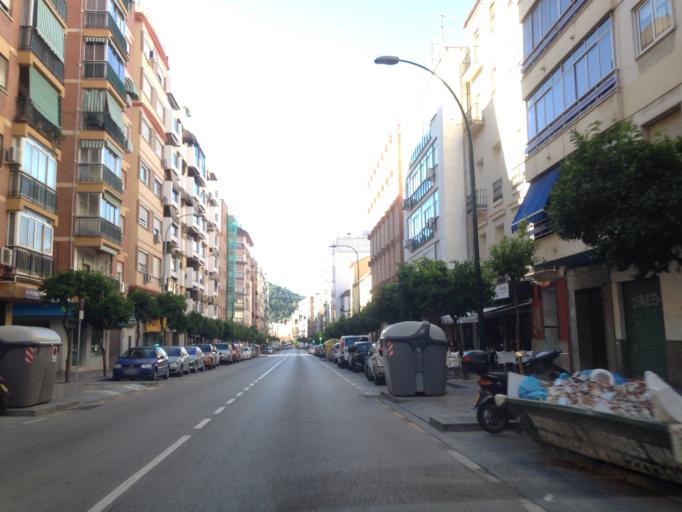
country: ES
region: Andalusia
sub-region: Provincia de Malaga
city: Malaga
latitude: 36.7324
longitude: -4.4155
